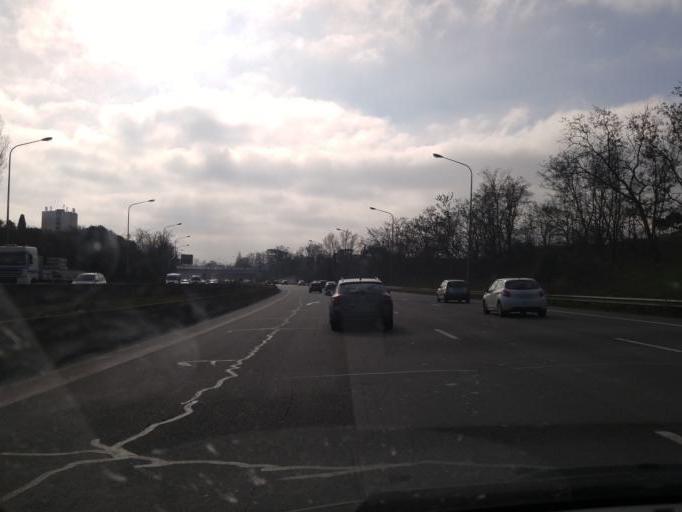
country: FR
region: Midi-Pyrenees
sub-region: Departement de la Haute-Garonne
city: Blagnac
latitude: 43.5995
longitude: 1.3974
